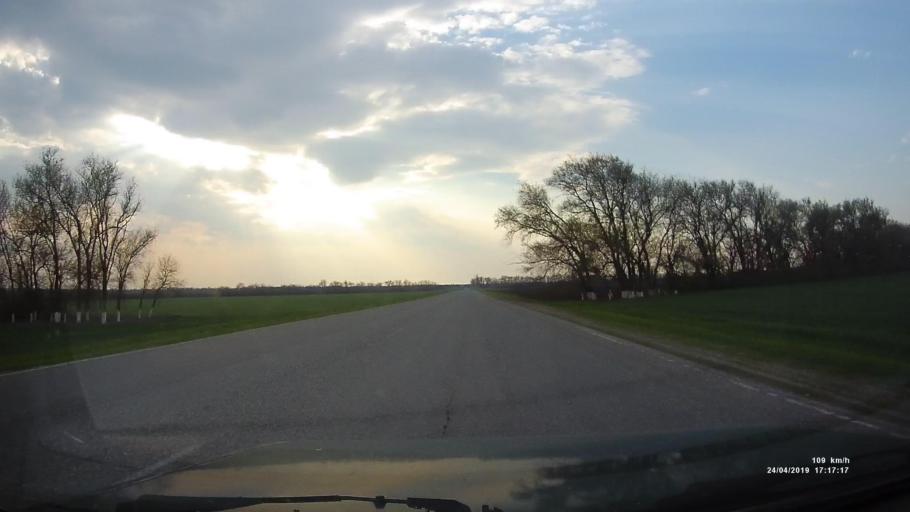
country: RU
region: Rostov
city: Gigant
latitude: 46.5057
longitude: 41.4064
